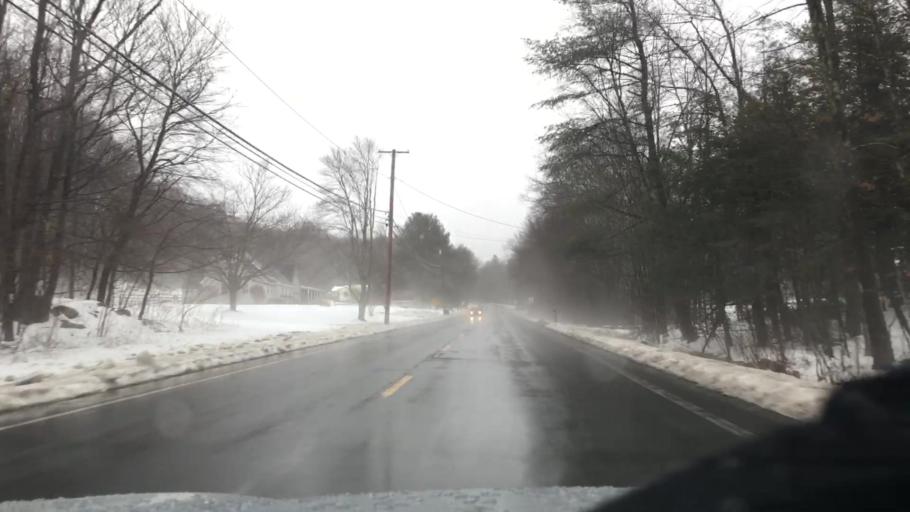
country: US
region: Massachusetts
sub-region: Hampshire County
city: Belchertown
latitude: 42.3001
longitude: -72.4068
